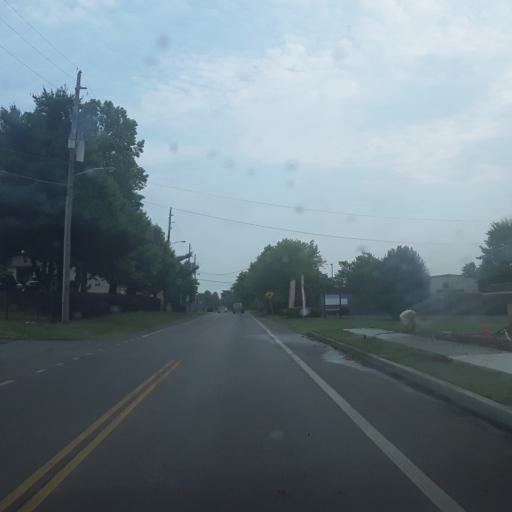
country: US
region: Tennessee
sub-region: Williamson County
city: Brentwood Estates
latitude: 36.0474
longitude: -86.7166
